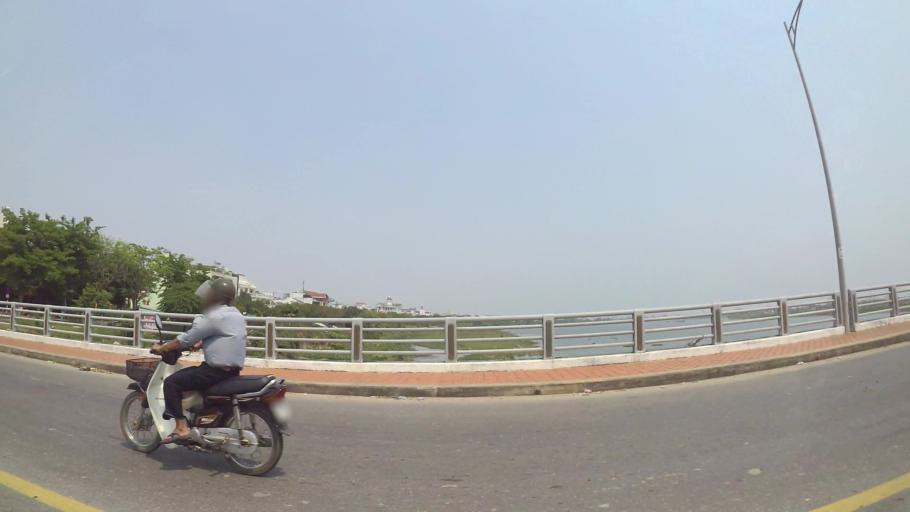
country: VN
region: Da Nang
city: Cam Le
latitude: 16.0248
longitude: 108.2224
